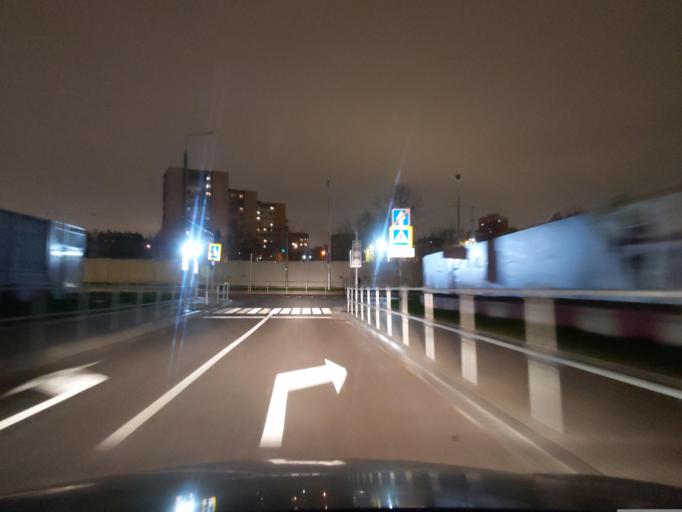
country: RU
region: Moskovskaya
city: Kozhukhovo
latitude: 55.6982
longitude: 37.6598
